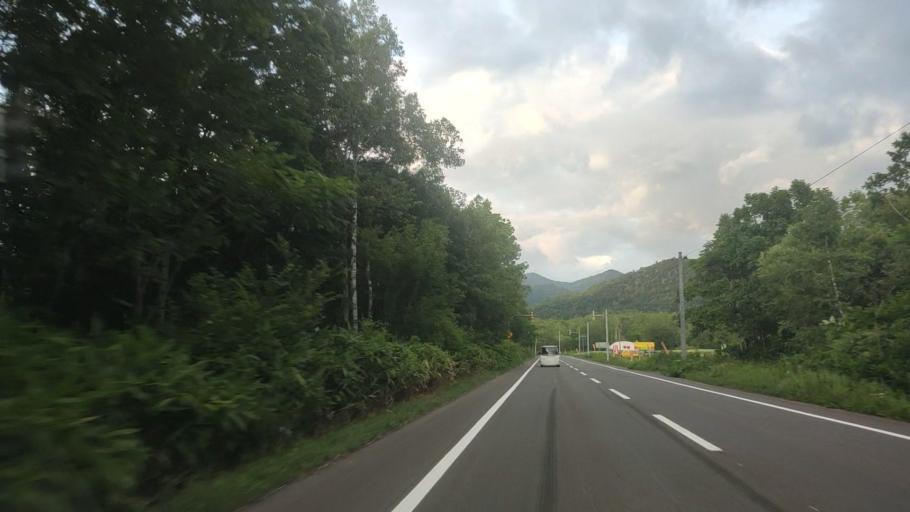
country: JP
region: Hokkaido
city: Ashibetsu
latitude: 43.3225
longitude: 142.1478
